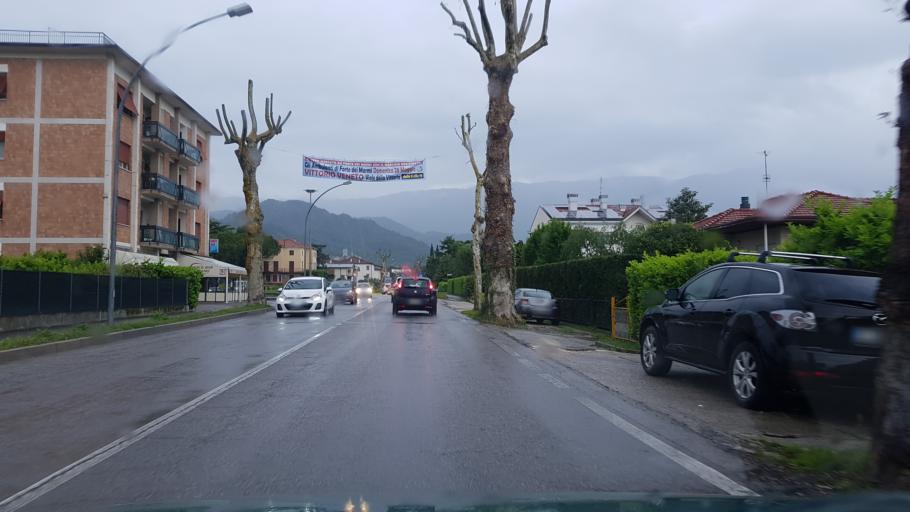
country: IT
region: Veneto
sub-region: Provincia di Treviso
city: Vittorio Veneto
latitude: 45.9705
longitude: 12.3129
